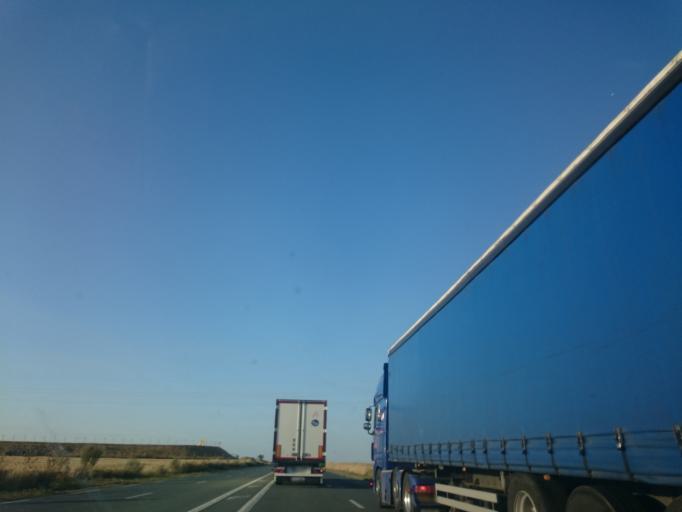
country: FR
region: Centre
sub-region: Departement du Loiret
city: Artenay
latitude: 48.0962
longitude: 1.8833
